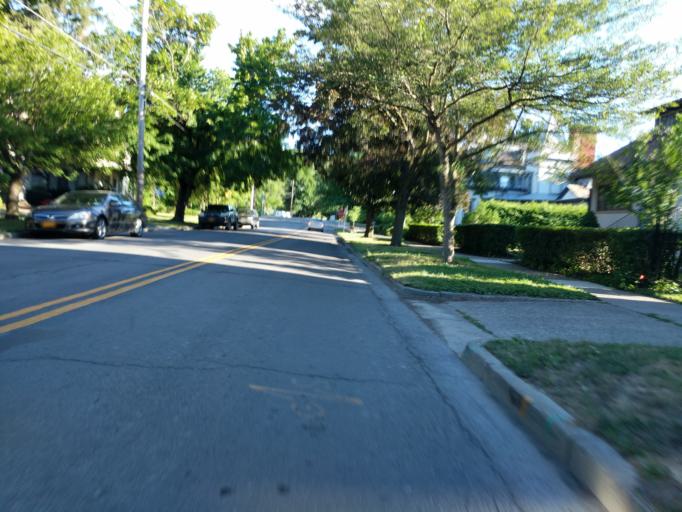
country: US
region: New York
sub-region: Tompkins County
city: Ithaca
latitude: 42.4353
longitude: -76.5017
